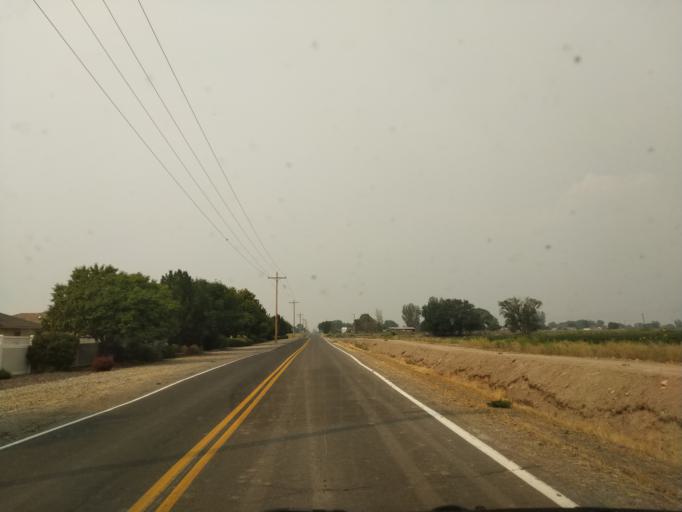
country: US
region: Colorado
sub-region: Mesa County
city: Fruitvale
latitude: 39.0318
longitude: -108.4967
